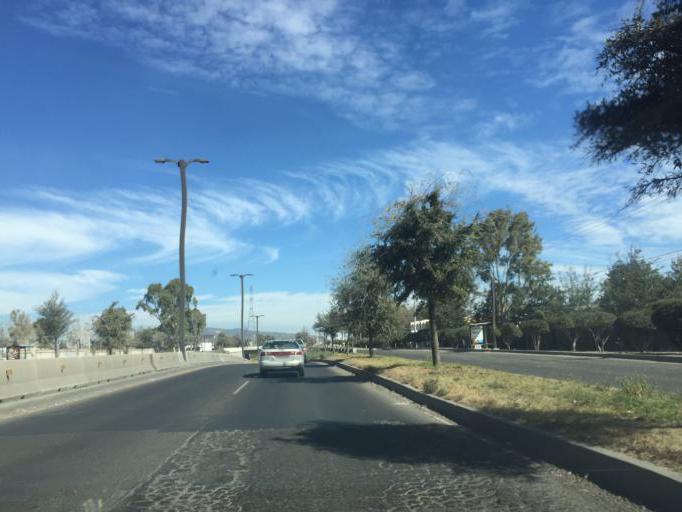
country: MX
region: Queretaro
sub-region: San Juan del Rio
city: Santa Cruz Escandon
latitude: 20.4155
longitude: -99.9809
